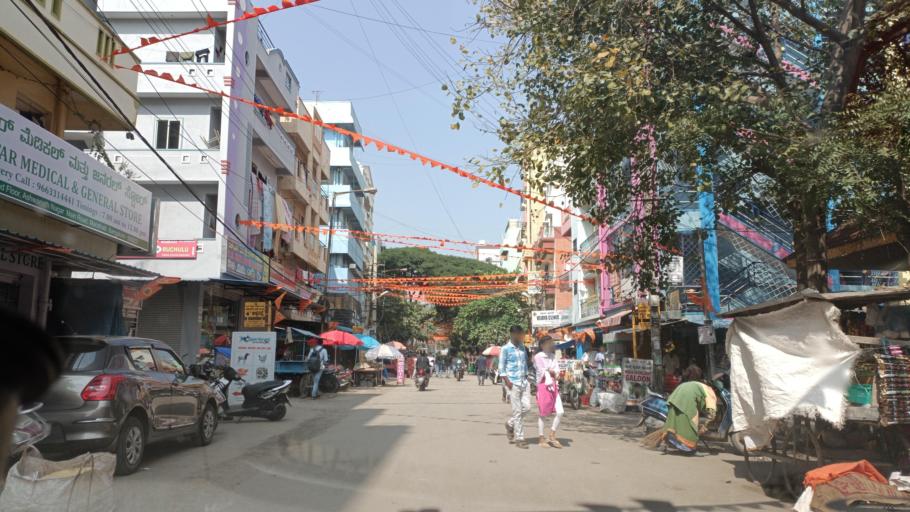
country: IN
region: Karnataka
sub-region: Bangalore Urban
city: Bangalore
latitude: 12.9582
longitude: 77.7028
